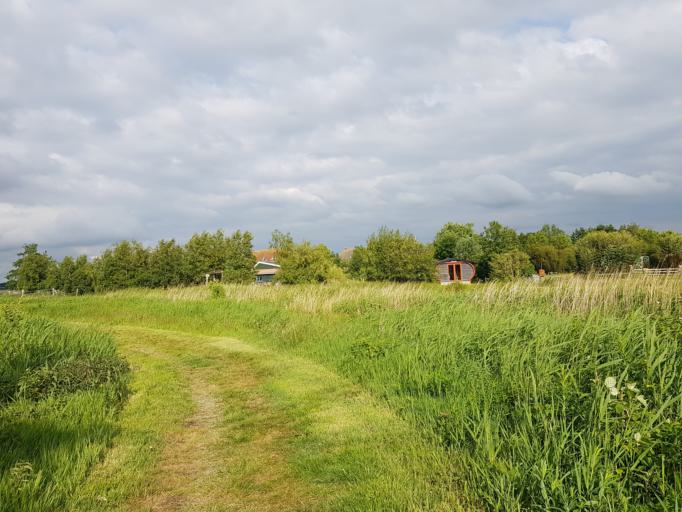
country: NL
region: Friesland
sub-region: Gemeente Smallingerland
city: Oudega
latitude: 53.0886
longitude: 5.9679
